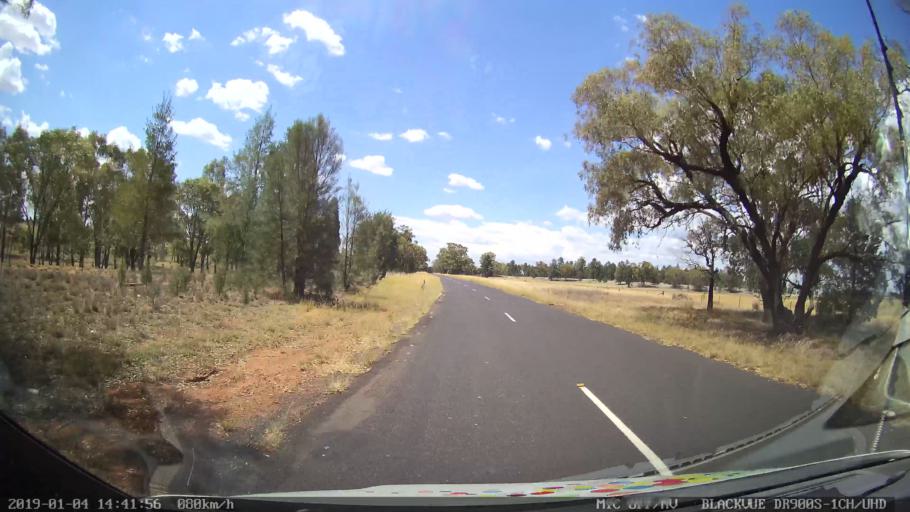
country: AU
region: New South Wales
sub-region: Dubbo Municipality
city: Dubbo
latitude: -32.1339
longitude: 148.6391
